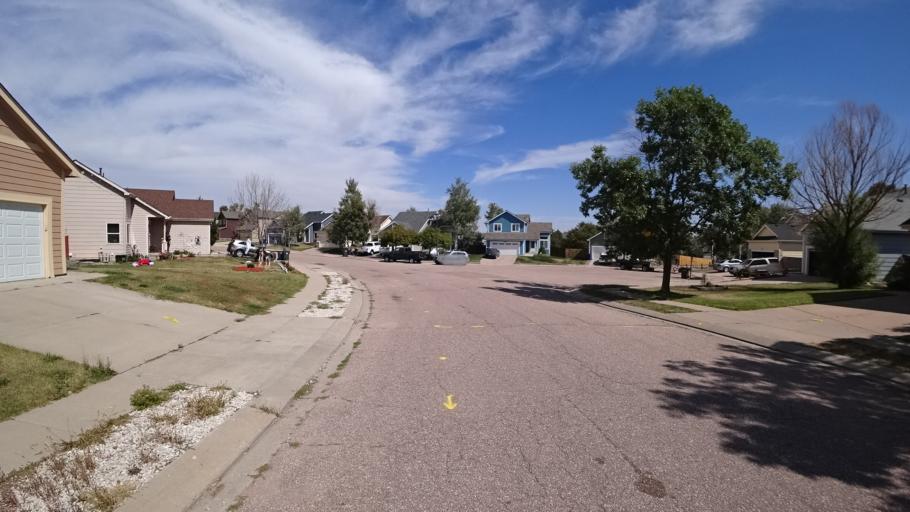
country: US
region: Colorado
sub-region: El Paso County
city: Cimarron Hills
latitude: 38.9000
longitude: -104.7108
